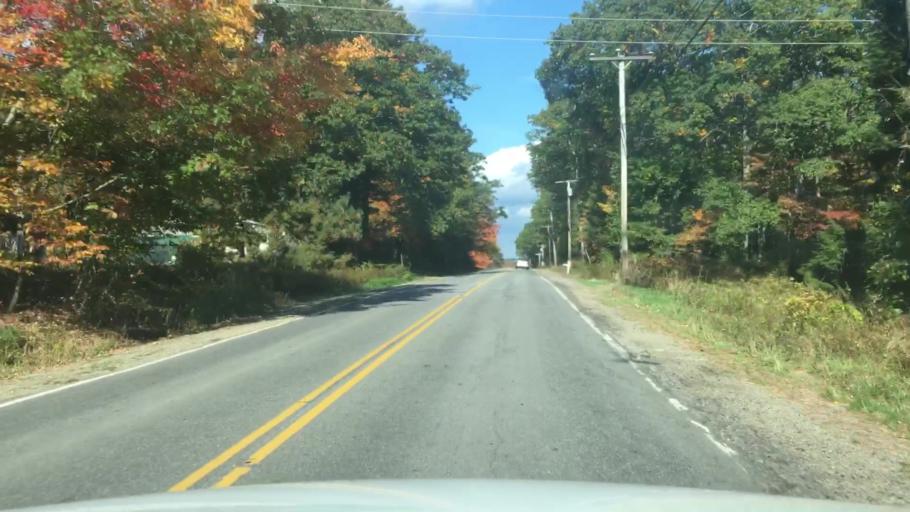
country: US
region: Maine
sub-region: Knox County
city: Warren
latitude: 44.1304
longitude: -69.2391
